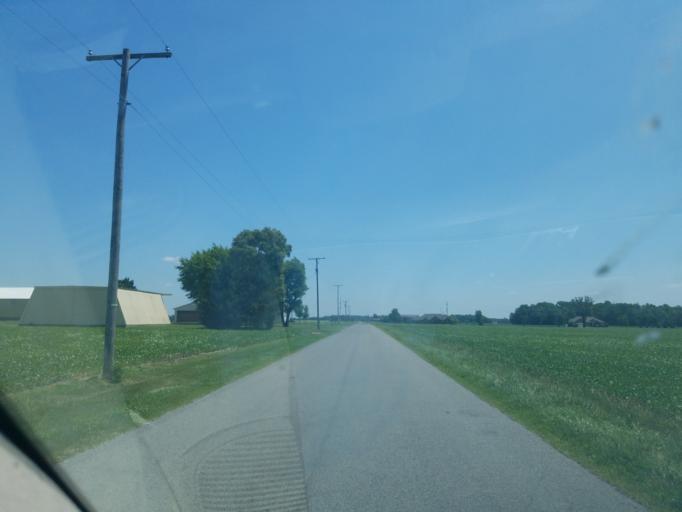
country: US
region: Ohio
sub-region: Allen County
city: Spencerville
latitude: 40.7576
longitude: -84.3627
